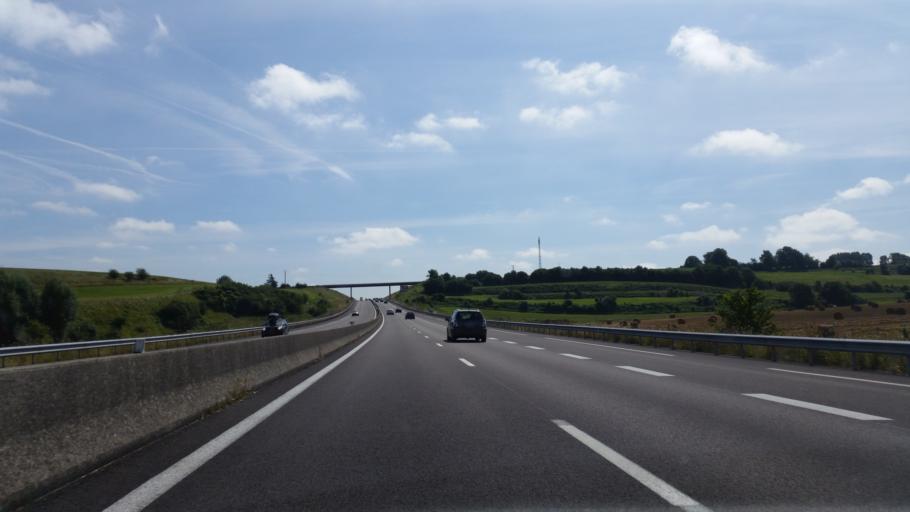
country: FR
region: Haute-Normandie
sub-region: Departement de la Seine-Maritime
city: Neufchatel-en-Bray
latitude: 49.7413
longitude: 1.5364
